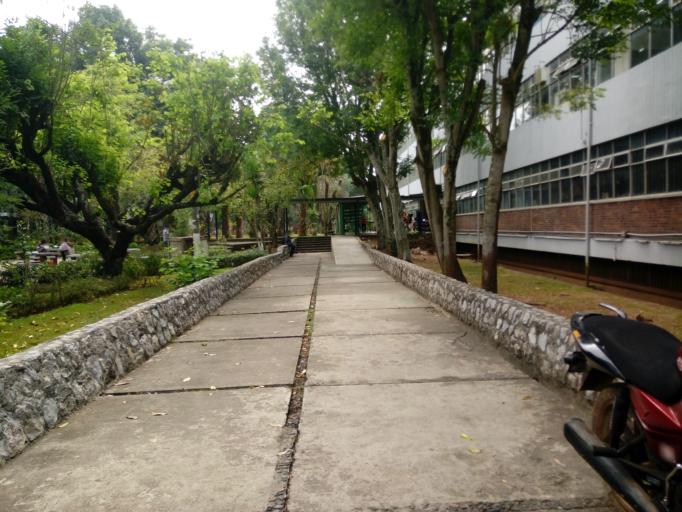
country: GT
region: Guatemala
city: Santa Catarina Pinula
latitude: 14.5853
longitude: -90.5539
